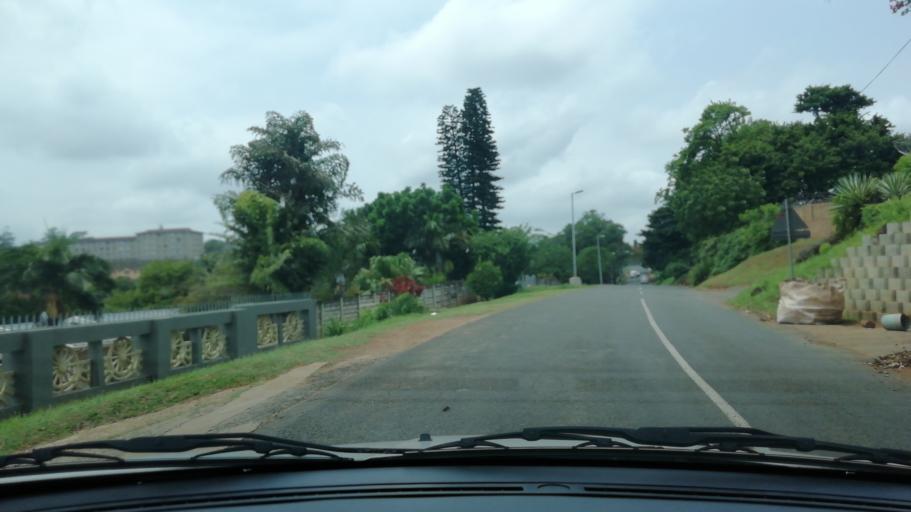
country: ZA
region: KwaZulu-Natal
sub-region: uThungulu District Municipality
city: Empangeni
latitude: -28.7512
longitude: 31.8901
